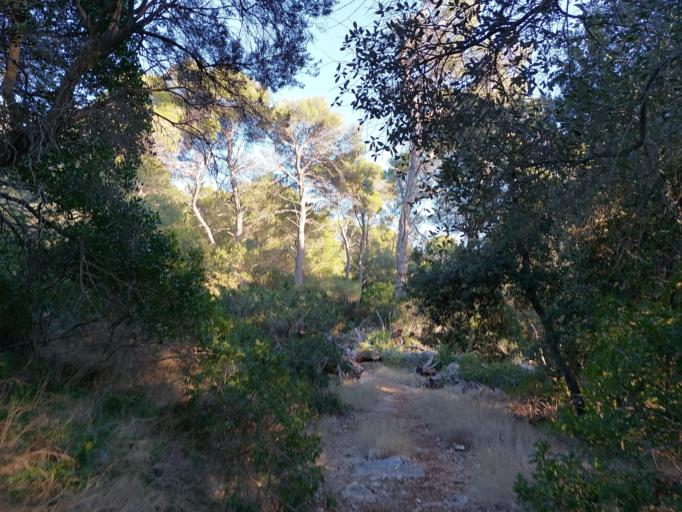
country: HR
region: Dubrovacko-Neretvanska
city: Smokvica
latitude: 42.7738
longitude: 16.7885
